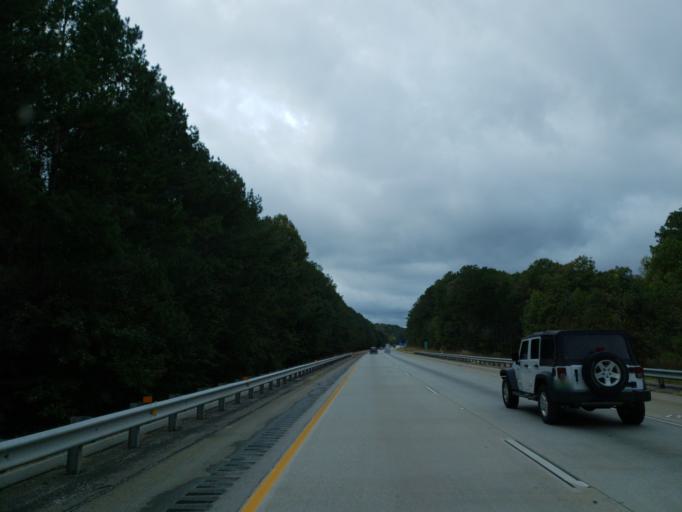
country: US
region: Georgia
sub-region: Carroll County
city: Mount Zion
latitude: 33.6888
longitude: -85.2215
